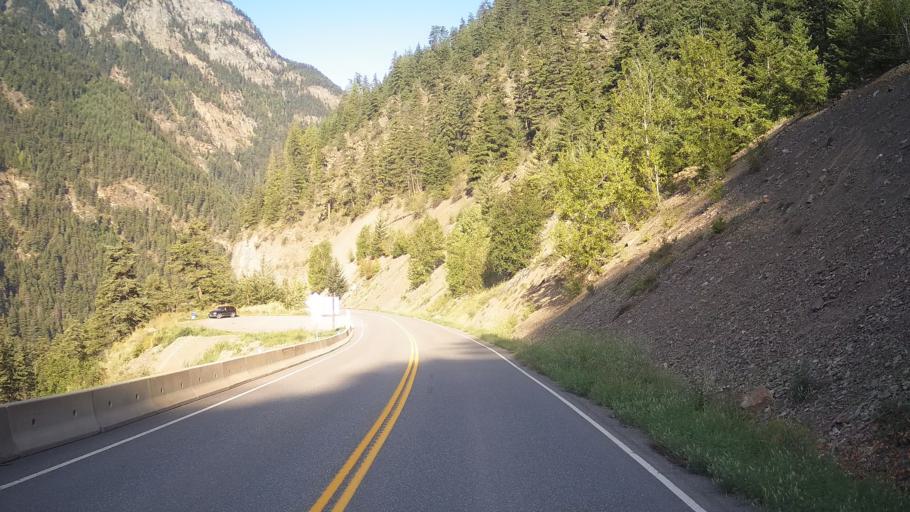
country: CA
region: British Columbia
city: Lillooet
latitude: 50.6430
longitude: -122.0318
